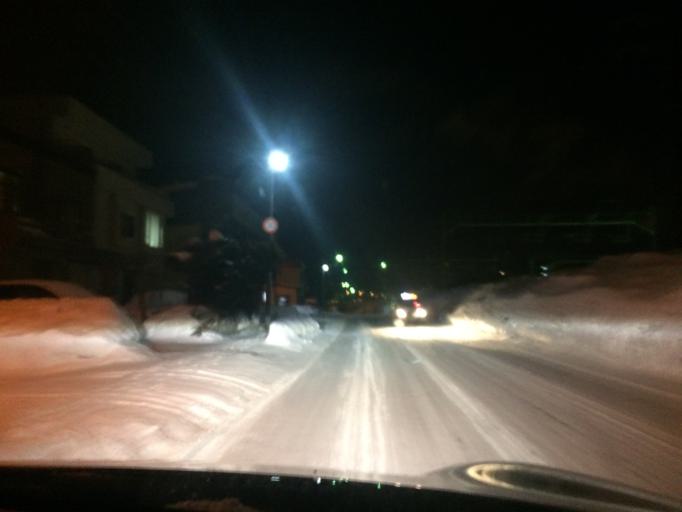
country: JP
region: Hokkaido
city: Sapporo
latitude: 43.0496
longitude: 141.4236
